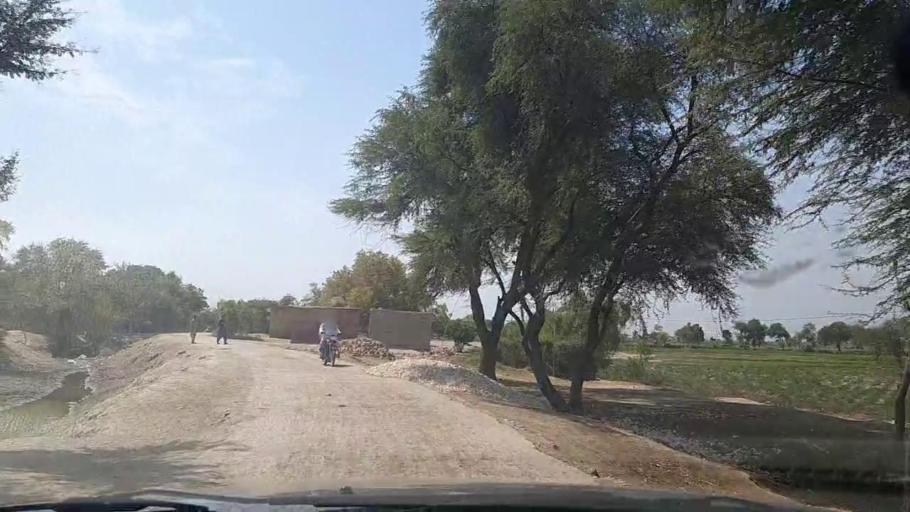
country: PK
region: Sindh
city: Mirpur Batoro
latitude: 24.6488
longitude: 68.1522
